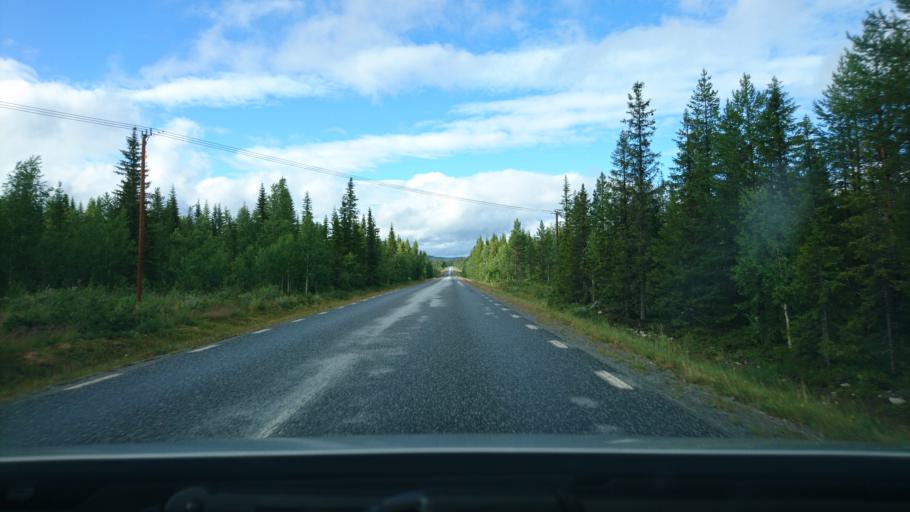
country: SE
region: Vaesterbotten
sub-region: Storumans Kommun
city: Storuman
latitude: 64.8658
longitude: 16.9918
